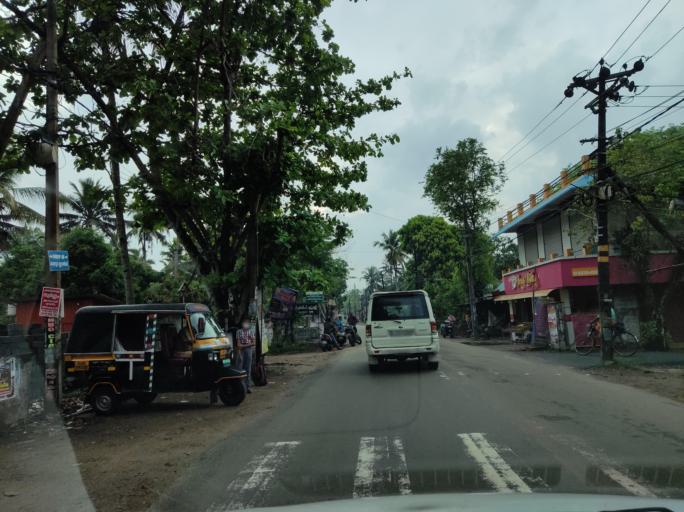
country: IN
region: Kerala
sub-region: Alappuzha
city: Kayankulam
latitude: 9.2584
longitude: 76.4305
